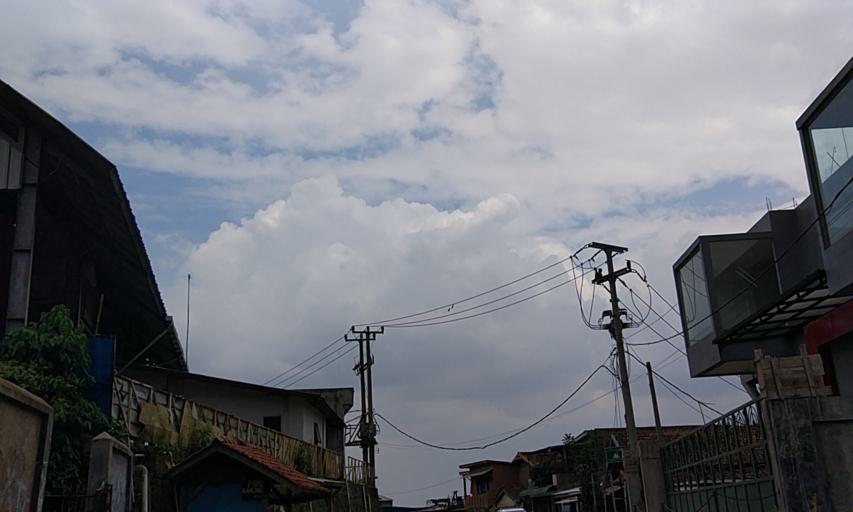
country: ID
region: West Java
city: Bandung
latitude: -6.8795
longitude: 107.6926
